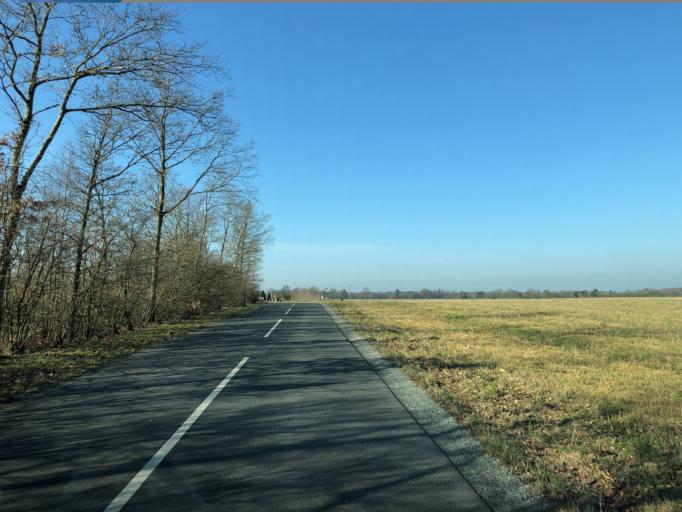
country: DK
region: Central Jutland
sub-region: Ikast-Brande Kommune
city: Bording Kirkeby
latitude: 56.1620
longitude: 9.3317
